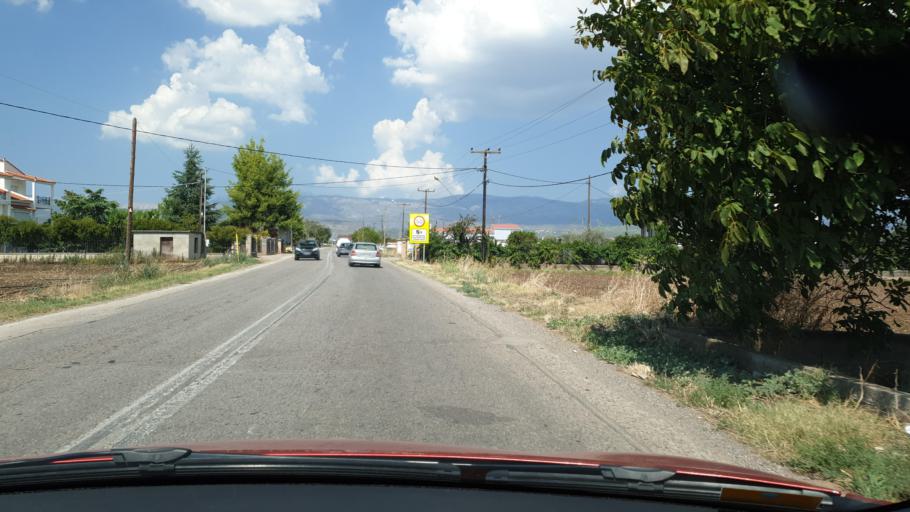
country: GR
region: Central Greece
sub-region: Nomos Evvoias
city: Kastella
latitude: 38.5522
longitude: 23.6314
